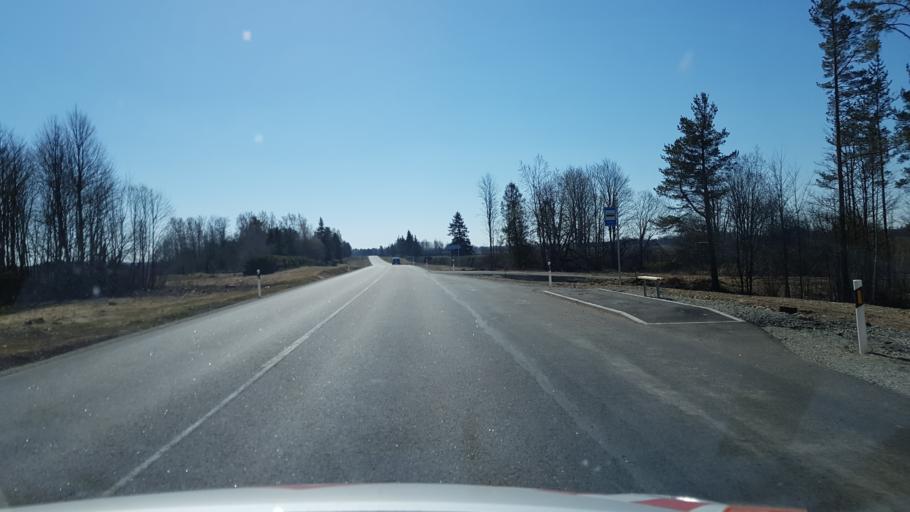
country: EE
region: Laeaene-Virumaa
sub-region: Vinni vald
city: Vinni
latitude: 59.0871
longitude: 26.6254
